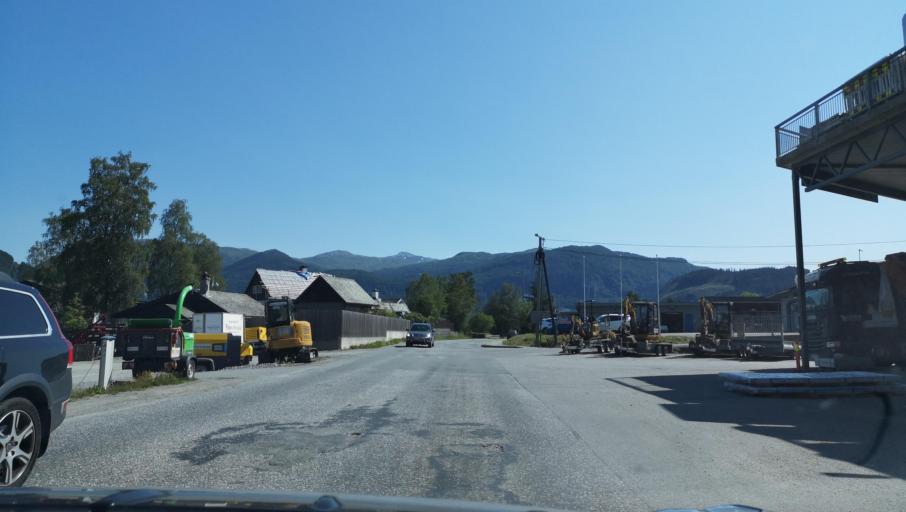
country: NO
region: Hordaland
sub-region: Voss
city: Voss
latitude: 60.6346
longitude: 6.4608
